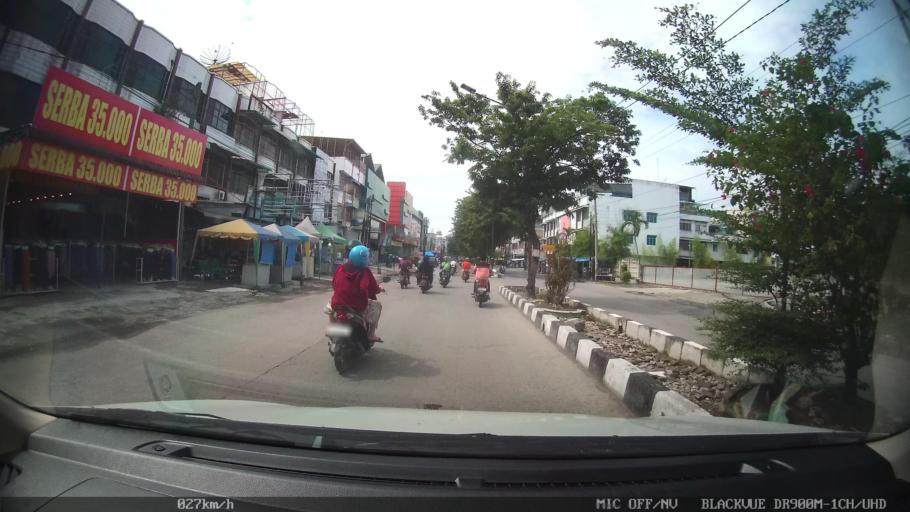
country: ID
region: North Sumatra
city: Medan
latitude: 3.5971
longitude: 98.7065
